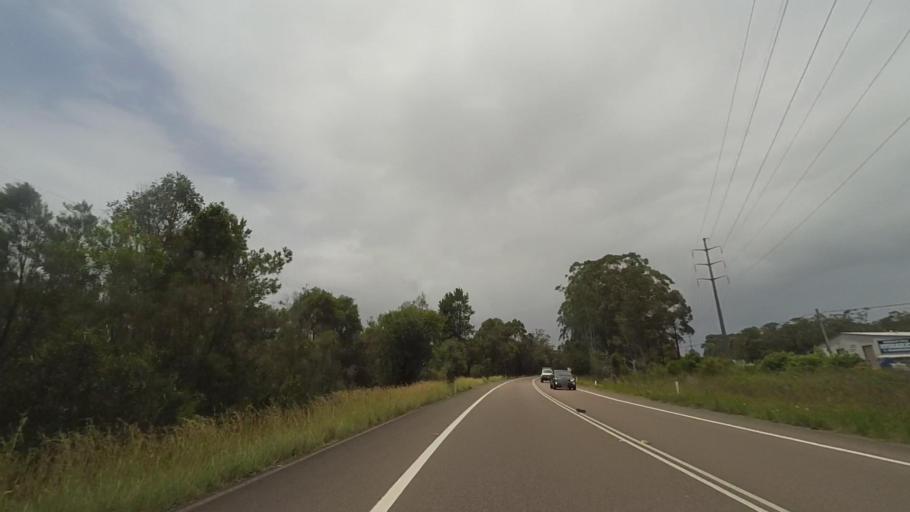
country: AU
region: New South Wales
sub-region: Wyong Shire
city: Chittaway Bay
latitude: -33.3300
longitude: 151.4069
